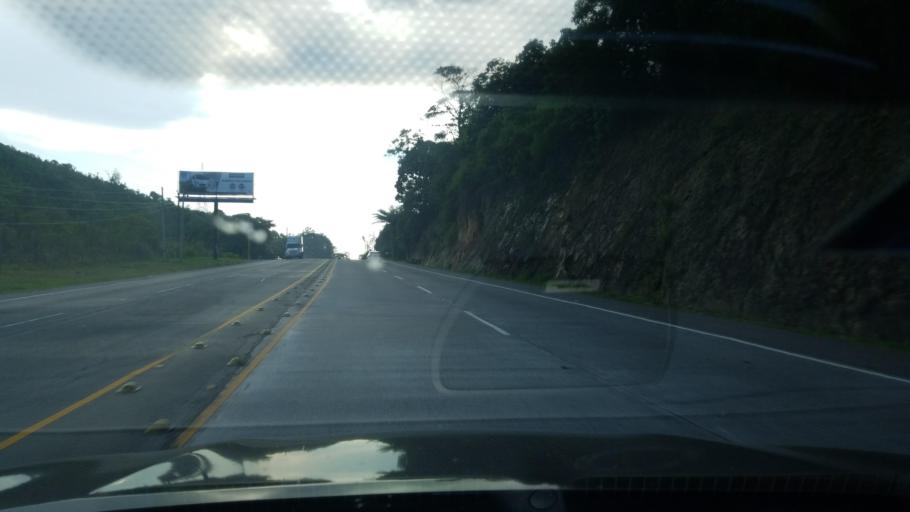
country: HN
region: Comayagua
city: El Socorro
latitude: 14.6596
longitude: -87.9448
